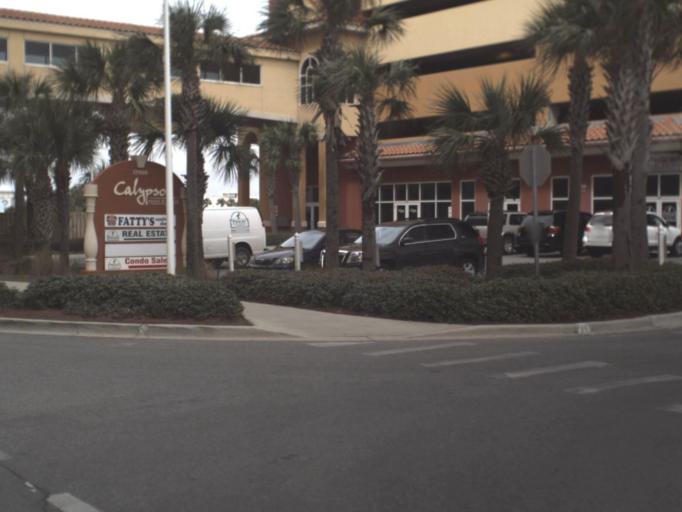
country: US
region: Florida
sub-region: Bay County
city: Laguna Beach
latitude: 30.2141
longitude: -85.8736
